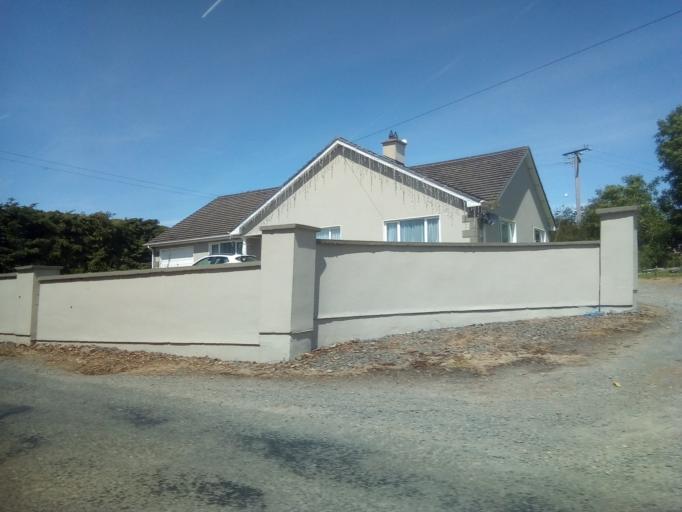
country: IE
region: Leinster
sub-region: Loch Garman
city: Loch Garman
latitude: 52.2353
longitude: -6.5804
